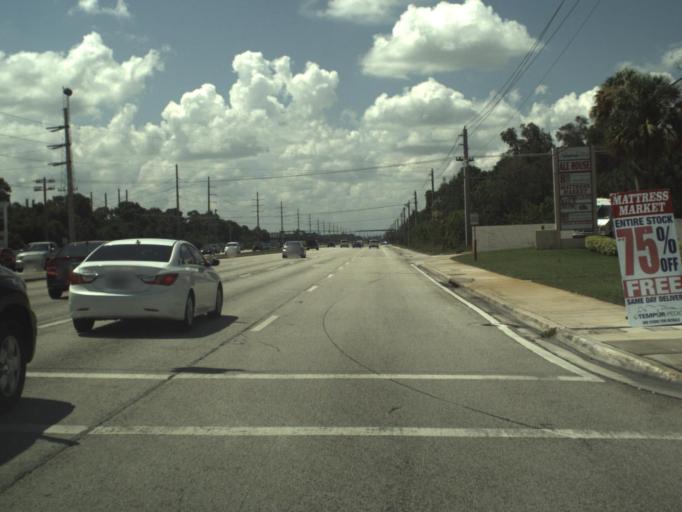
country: US
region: Florida
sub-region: Martin County
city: North River Shores
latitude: 27.2484
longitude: -80.2738
